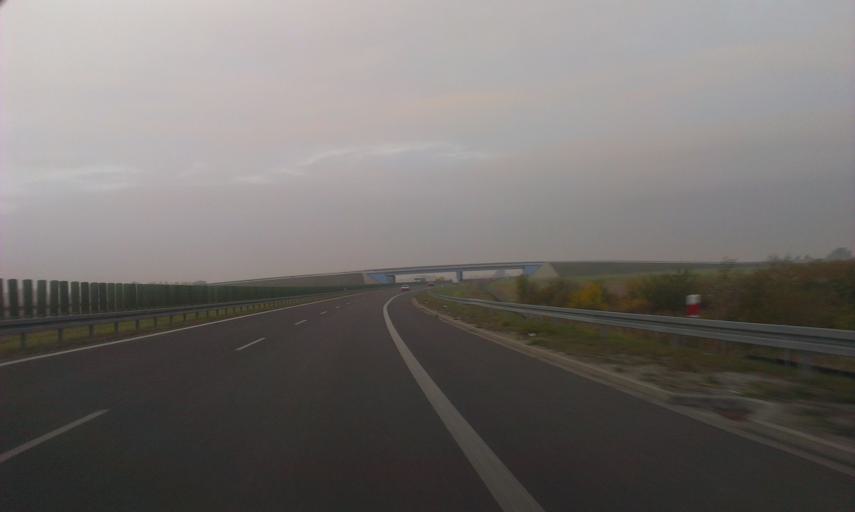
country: PL
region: Greater Poland Voivodeship
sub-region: Powiat poznanski
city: Zlotniki
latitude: 52.5151
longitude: 16.8265
